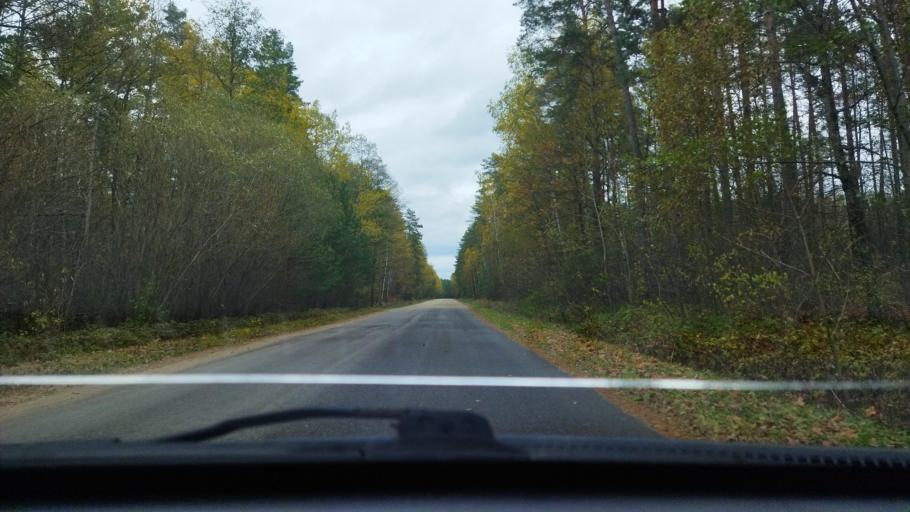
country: BY
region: Minsk
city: Svir
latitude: 54.8038
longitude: 26.2463
